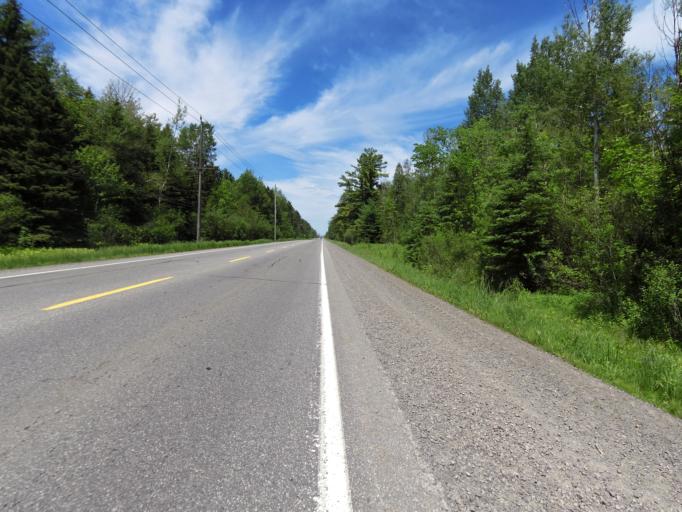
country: CA
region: Ontario
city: Ottawa
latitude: 45.3592
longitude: -75.5889
